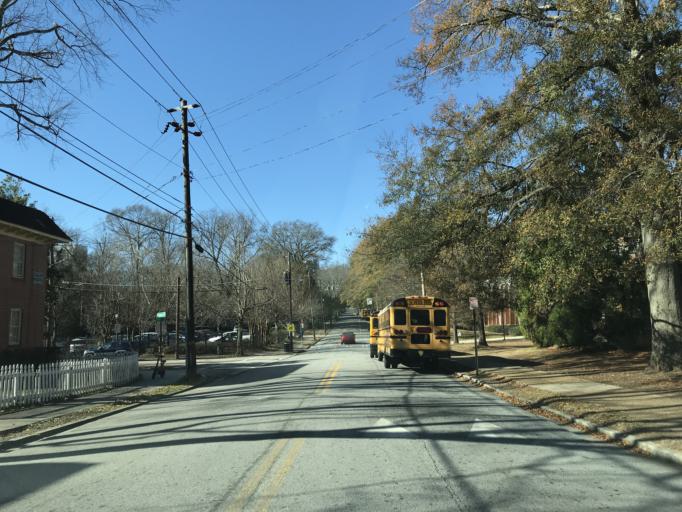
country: US
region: Georgia
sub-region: DeKalb County
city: Druid Hills
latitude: 33.7795
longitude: -84.3707
